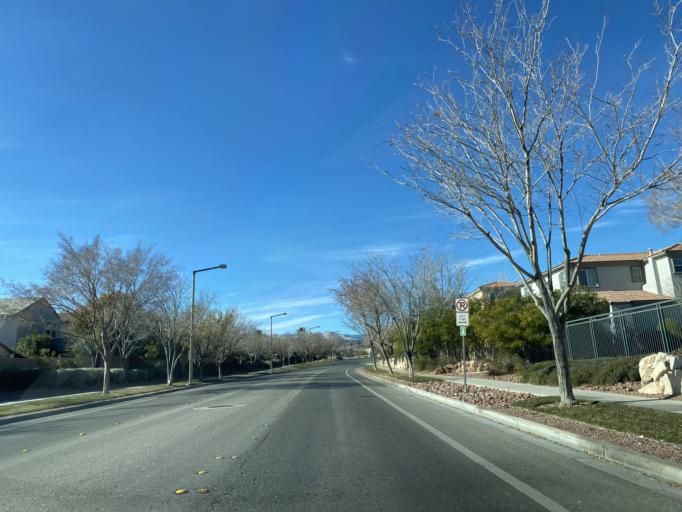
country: US
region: Nevada
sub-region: Clark County
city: Summerlin South
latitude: 36.1467
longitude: -115.3236
